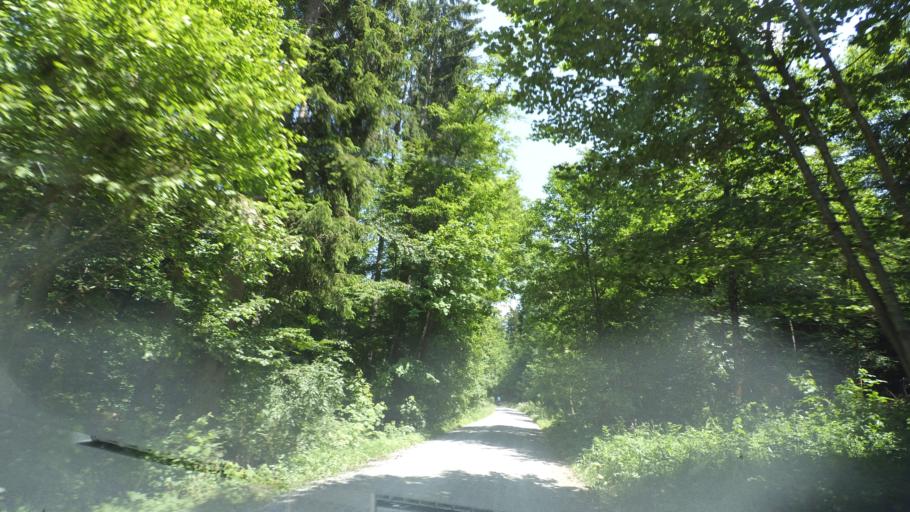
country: DE
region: Baden-Wuerttemberg
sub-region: Regierungsbezirk Stuttgart
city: Fichtenberg
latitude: 48.9719
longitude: 9.7079
